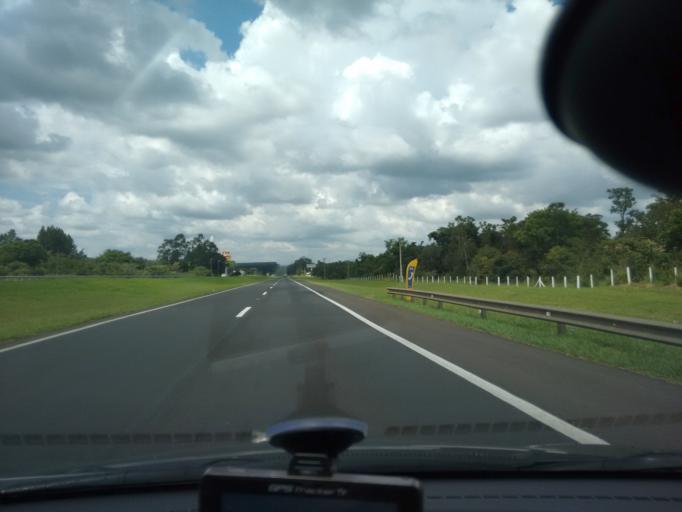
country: BR
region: Sao Paulo
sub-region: Sao Carlos
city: Sao Carlos
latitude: -22.0989
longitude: -47.8274
